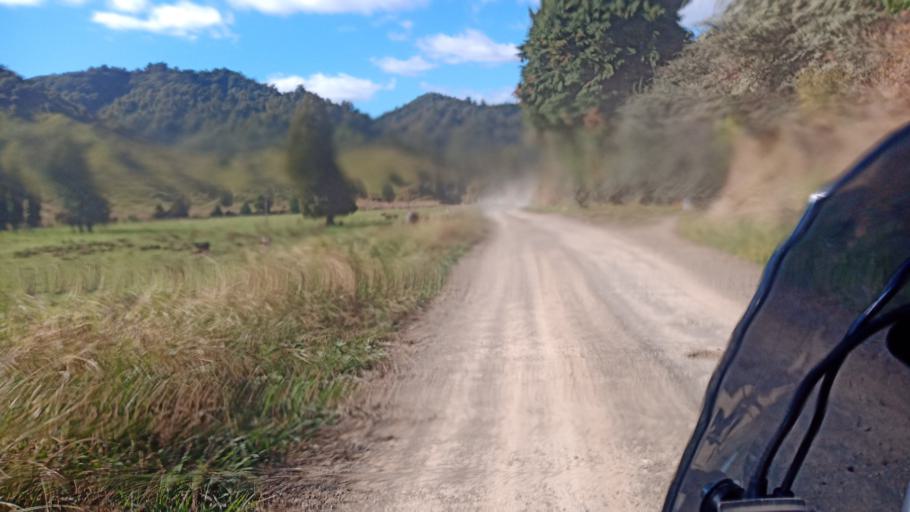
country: NZ
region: Bay of Plenty
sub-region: Opotiki District
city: Opotiki
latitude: -38.2526
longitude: 177.5818
